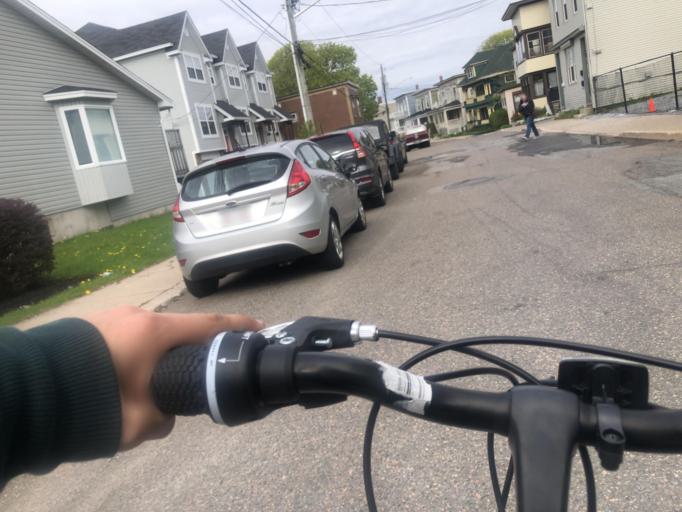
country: CA
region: New Brunswick
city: Saint John
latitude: 45.2744
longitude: -66.0788
